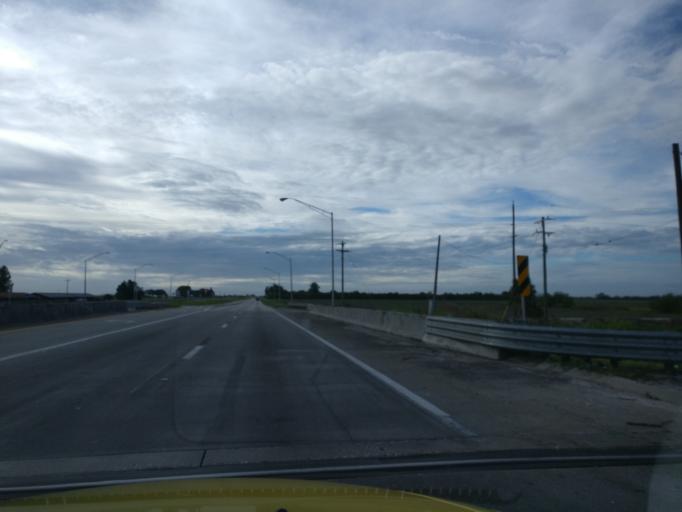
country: US
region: Florida
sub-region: Hendry County
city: Harlem
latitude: 26.7543
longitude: -80.9591
